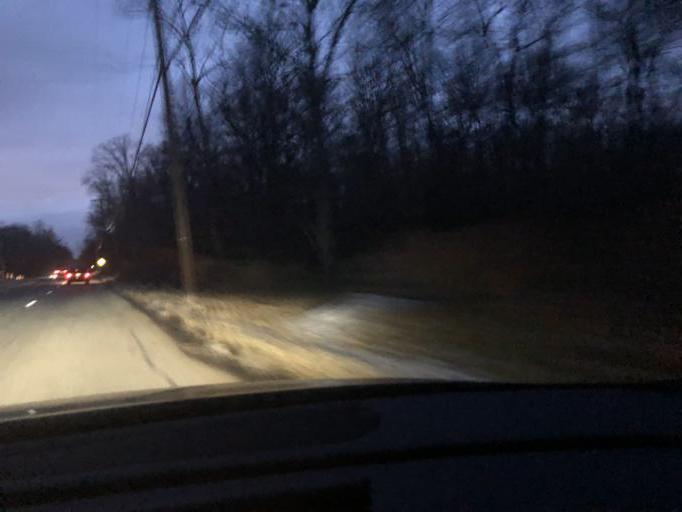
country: US
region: New Jersey
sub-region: Essex County
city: Northfield
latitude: 40.7689
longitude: -74.3466
